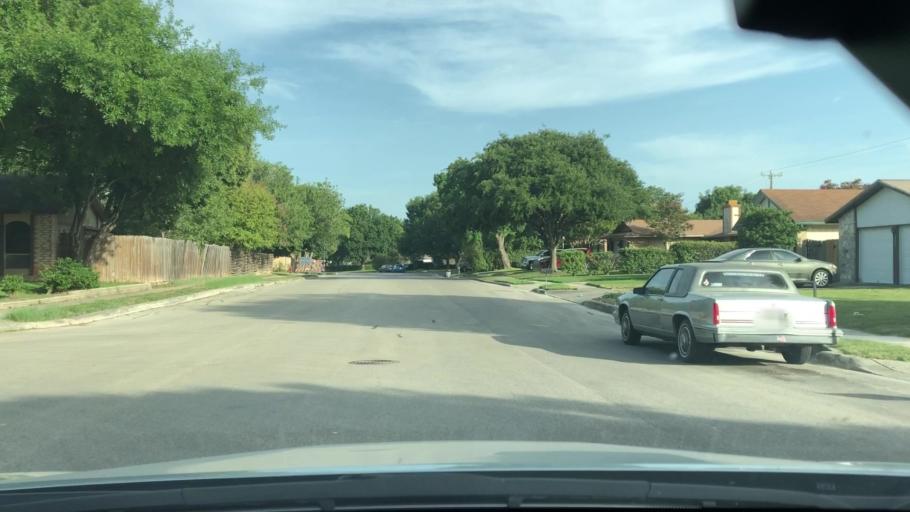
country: US
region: Texas
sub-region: Bexar County
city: Converse
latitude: 29.5354
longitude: -98.3241
